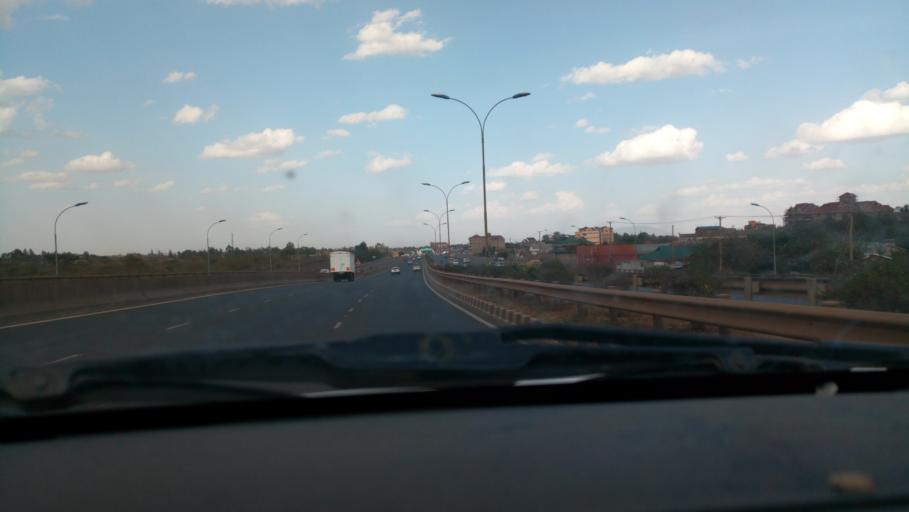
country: KE
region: Nairobi Area
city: Thika
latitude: -1.1325
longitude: 36.9753
